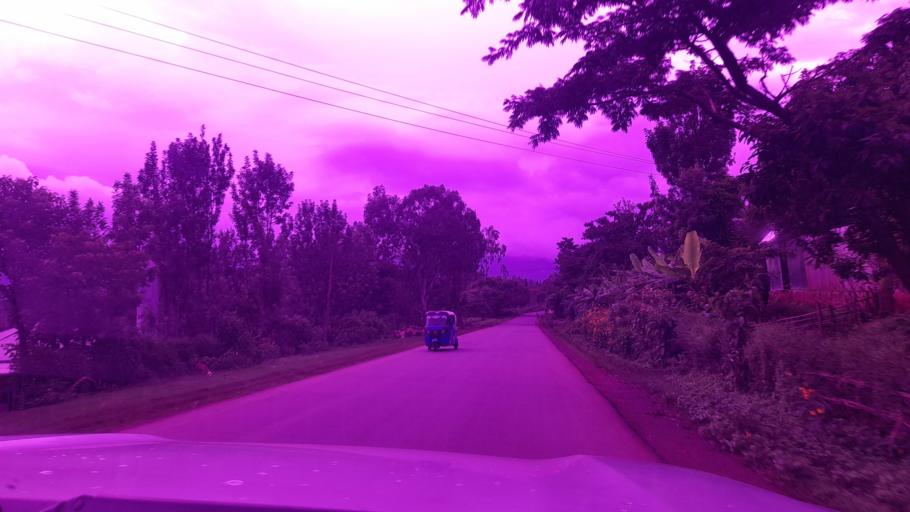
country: ET
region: Oromiya
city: Jima
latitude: 7.8911
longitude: 37.3892
